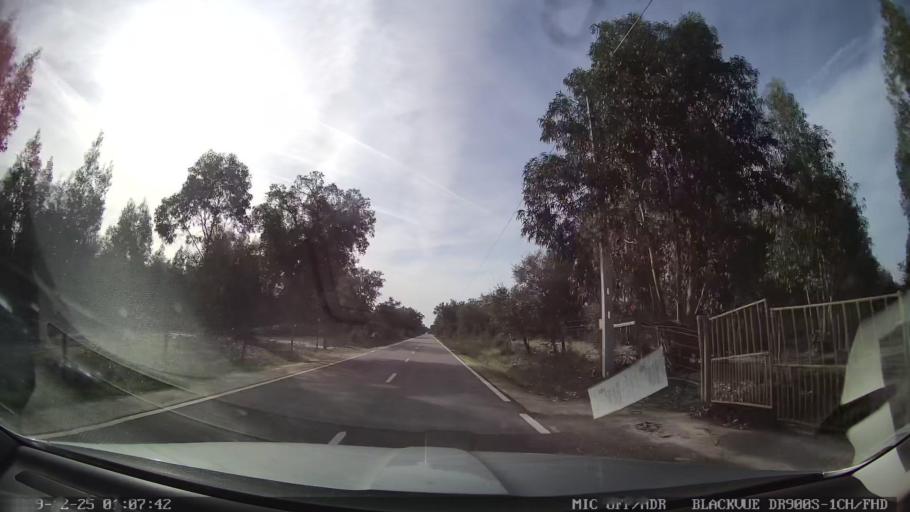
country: PT
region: Portalegre
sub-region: Nisa
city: Nisa
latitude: 39.4591
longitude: -7.7048
